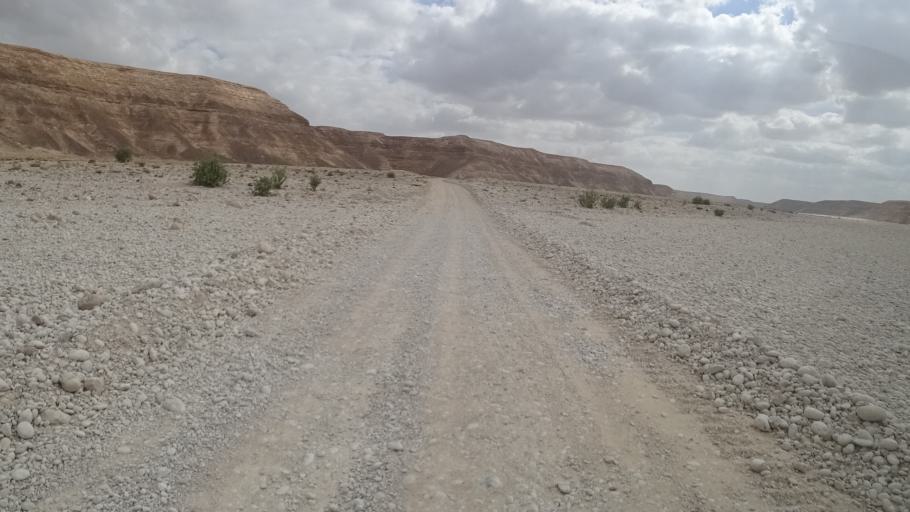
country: YE
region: Al Mahrah
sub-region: Shahan
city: Shihan as Sufla
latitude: 17.4639
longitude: 53.0070
